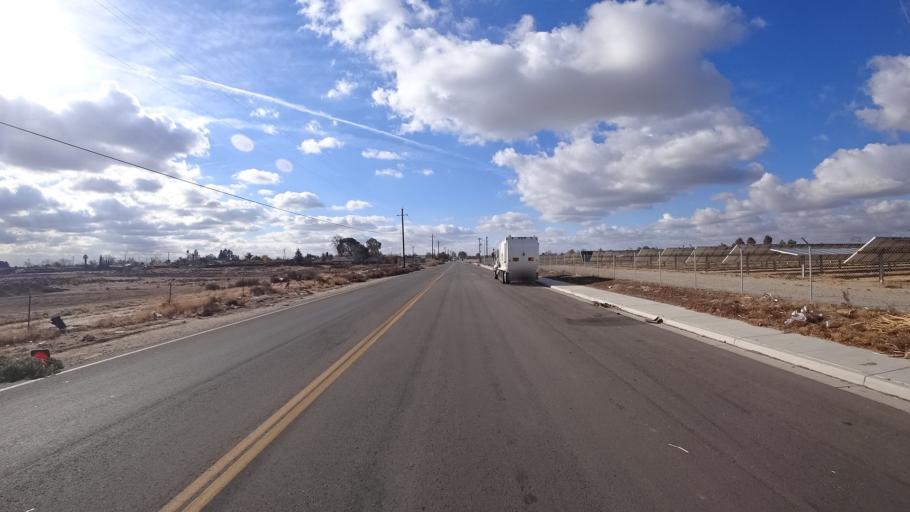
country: US
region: California
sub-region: Kern County
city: Greenfield
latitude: 35.3250
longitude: -118.9791
